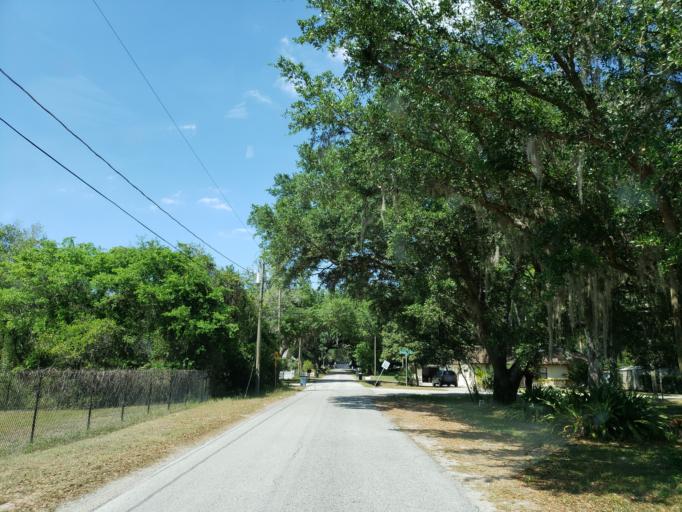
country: US
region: Florida
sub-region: Hillsborough County
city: Plant City
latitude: 28.0230
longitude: -82.1321
